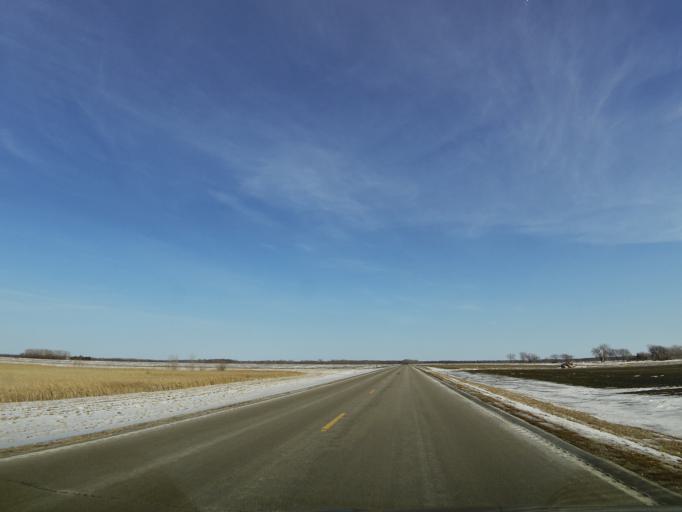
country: US
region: North Dakota
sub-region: Walsh County
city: Grafton
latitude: 48.4121
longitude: -97.1823
